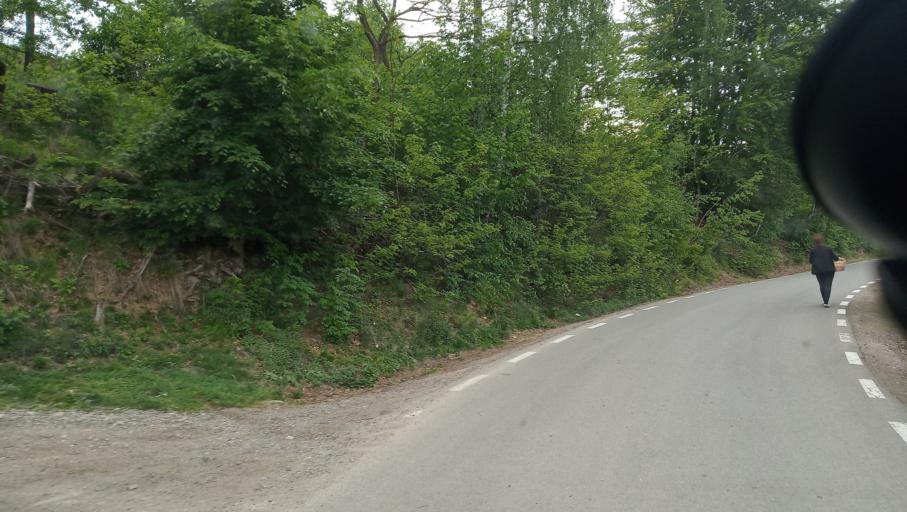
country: RO
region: Alba
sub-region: Comuna Horea
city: Horea
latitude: 46.5047
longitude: 22.9094
